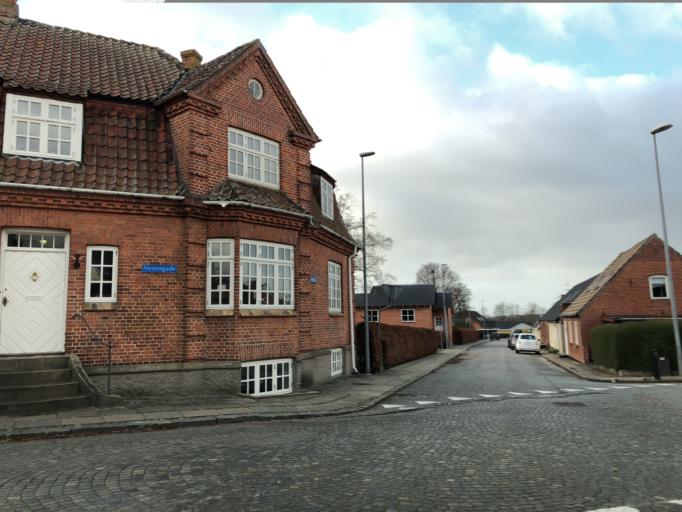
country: DK
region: Central Jutland
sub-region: Herning Kommune
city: Vildbjerg
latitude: 56.1993
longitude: 8.7649
